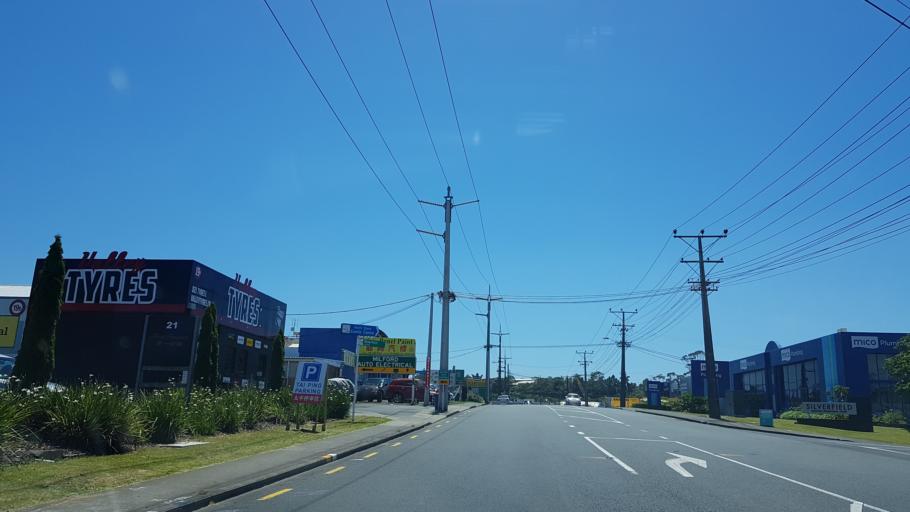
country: NZ
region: Auckland
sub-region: Auckland
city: North Shore
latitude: -36.7814
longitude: 174.7428
